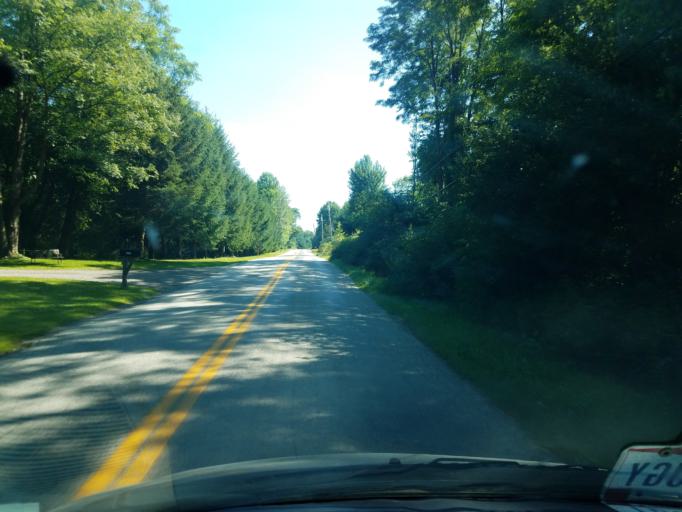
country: US
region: Ohio
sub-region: Portage County
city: Mantua
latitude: 41.3234
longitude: -81.2014
